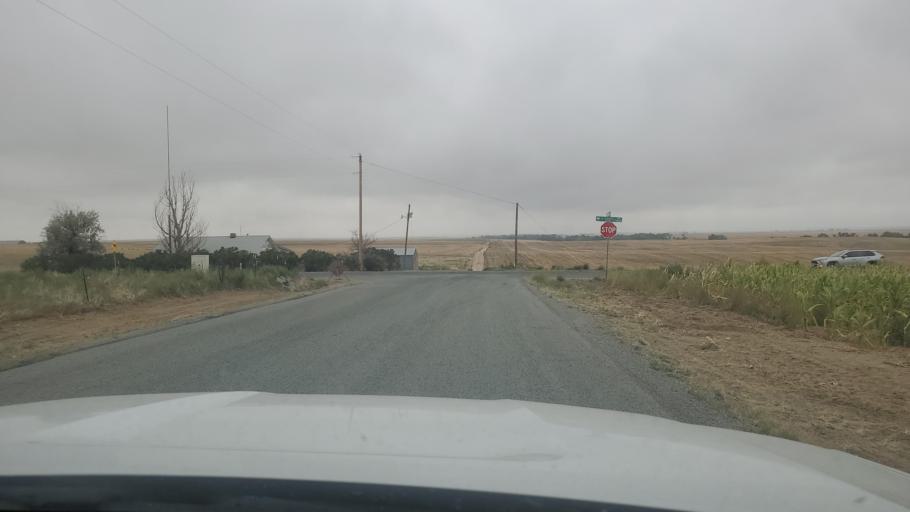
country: US
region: Colorado
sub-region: Weld County
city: Lochbuie
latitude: 39.9140
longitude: -104.6027
